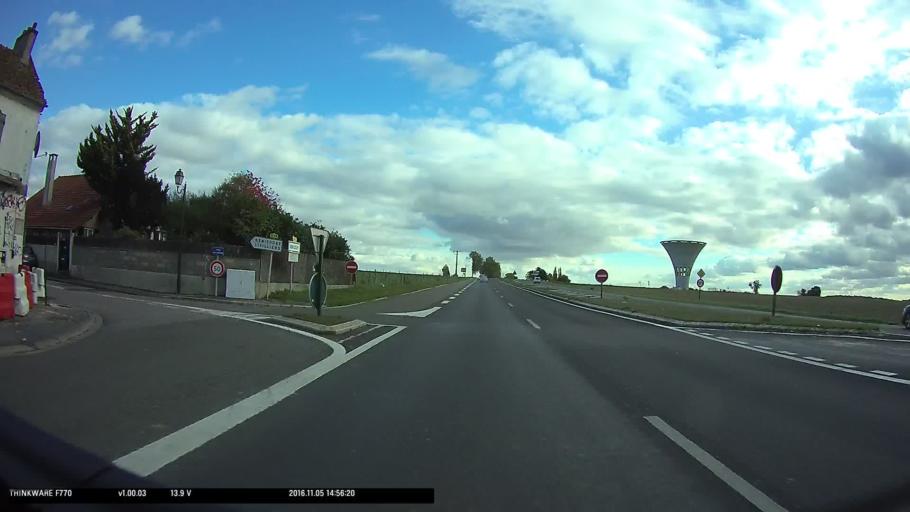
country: FR
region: Ile-de-France
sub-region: Departement du Val-d'Oise
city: Osny
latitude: 49.0864
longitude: 2.0637
